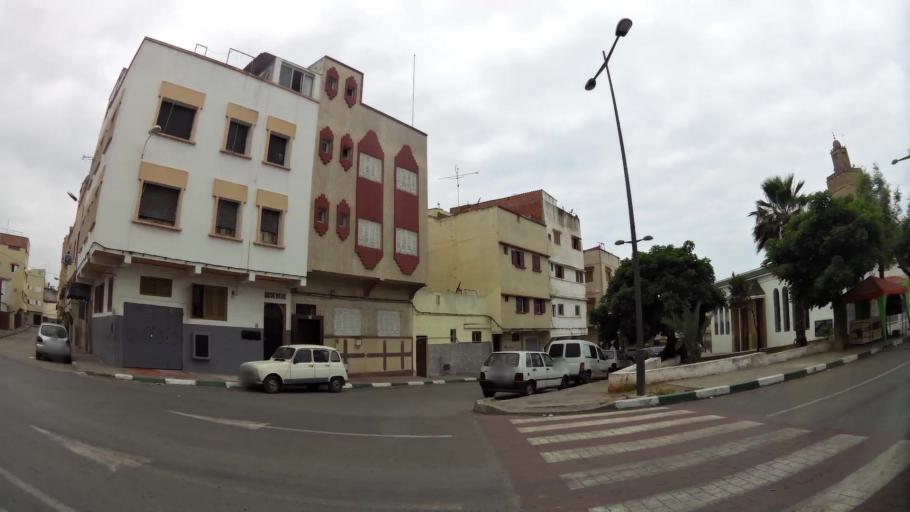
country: MA
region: Rabat-Sale-Zemmour-Zaer
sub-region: Rabat
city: Rabat
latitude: 33.9932
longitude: -6.8686
